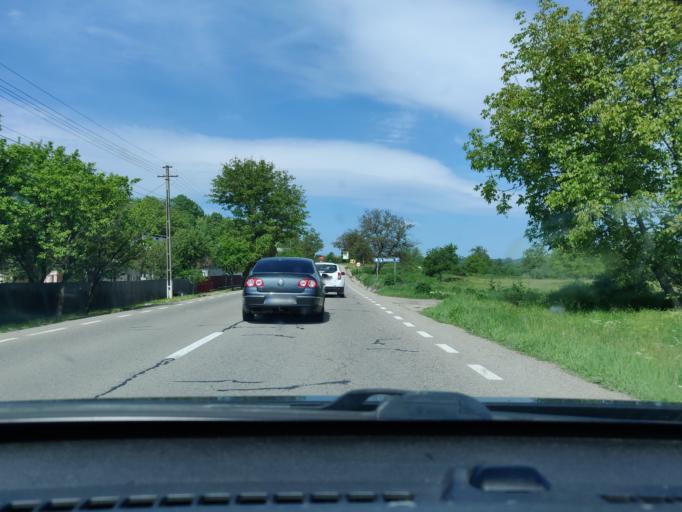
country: RO
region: Vrancea
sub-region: Comuna Vidra
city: Burca
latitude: 45.9049
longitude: 26.9699
